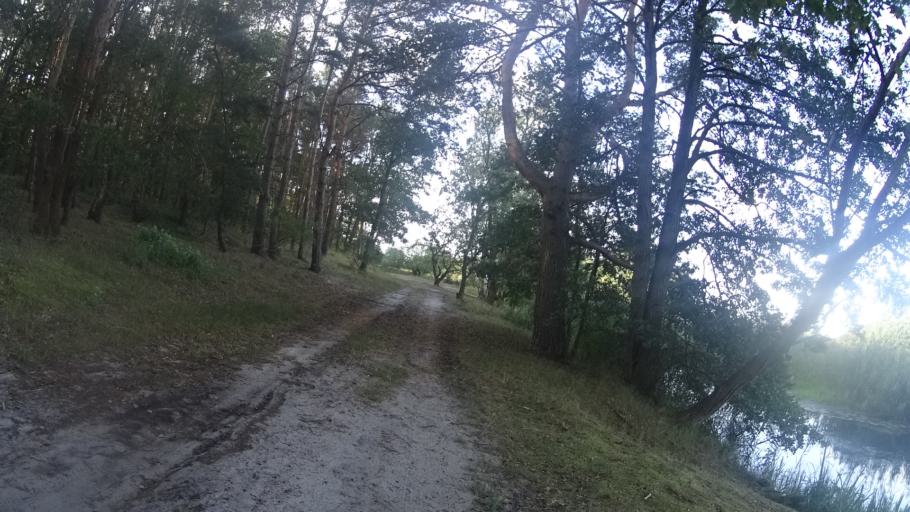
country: DE
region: Brandenburg
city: Premnitz
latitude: 52.5510
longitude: 12.3260
